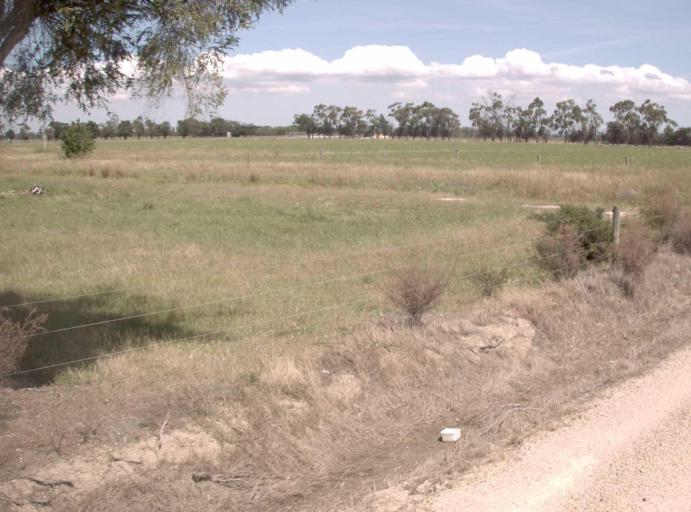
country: AU
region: Victoria
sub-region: Wellington
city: Heyfield
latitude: -38.0392
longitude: 146.8775
